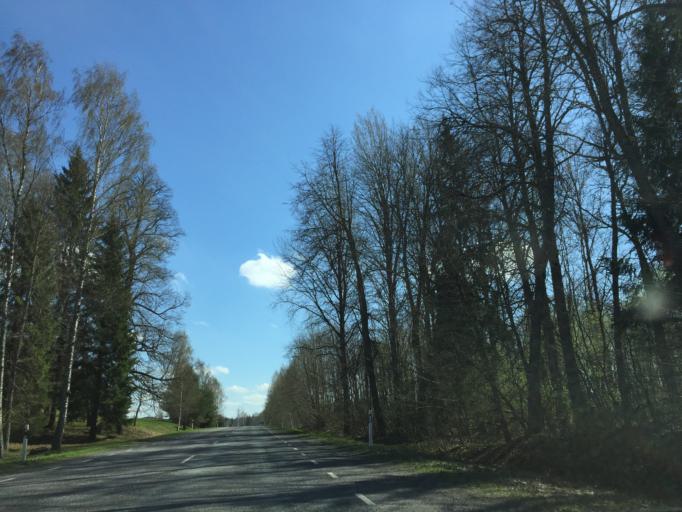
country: EE
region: Tartu
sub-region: Elva linn
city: Elva
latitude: 58.1507
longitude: 26.2255
